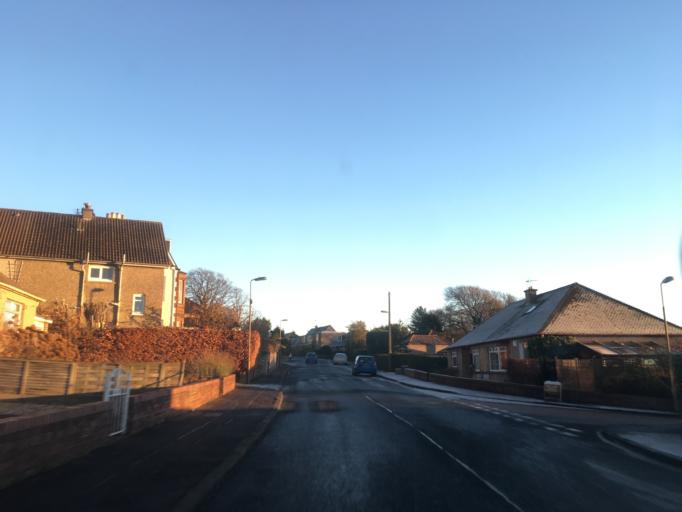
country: GB
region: Scotland
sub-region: Edinburgh
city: Colinton
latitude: 55.9481
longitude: -3.2828
